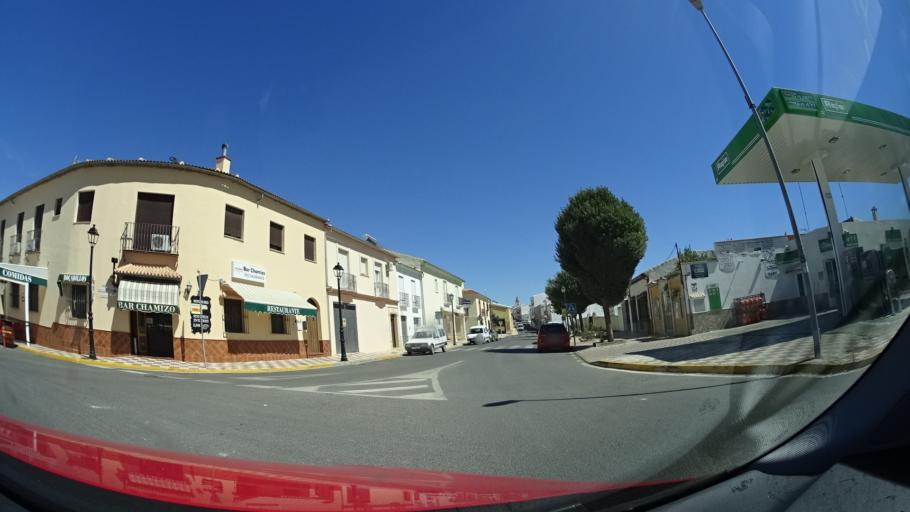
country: ES
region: Andalusia
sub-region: Provincia de Malaga
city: Sierra de Yeguas
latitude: 37.1239
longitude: -4.8732
